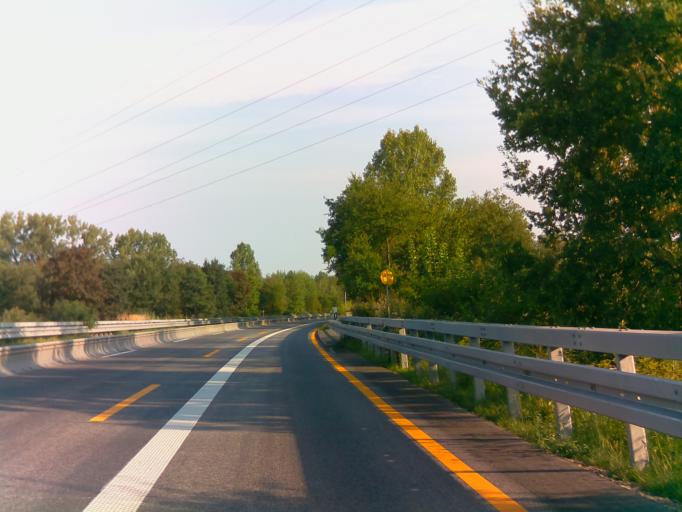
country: DE
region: Hesse
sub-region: Regierungsbezirk Darmstadt
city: Eppertshausen
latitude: 49.9373
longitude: 8.8423
